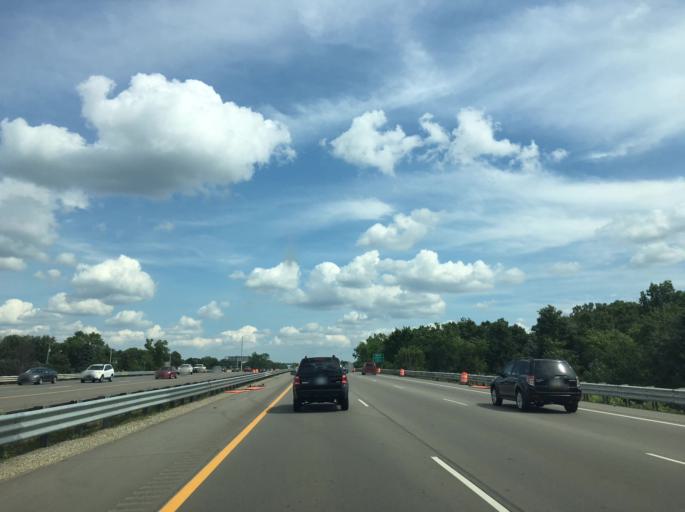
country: US
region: Michigan
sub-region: Oakland County
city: Waterford
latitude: 42.7225
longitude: -83.3515
